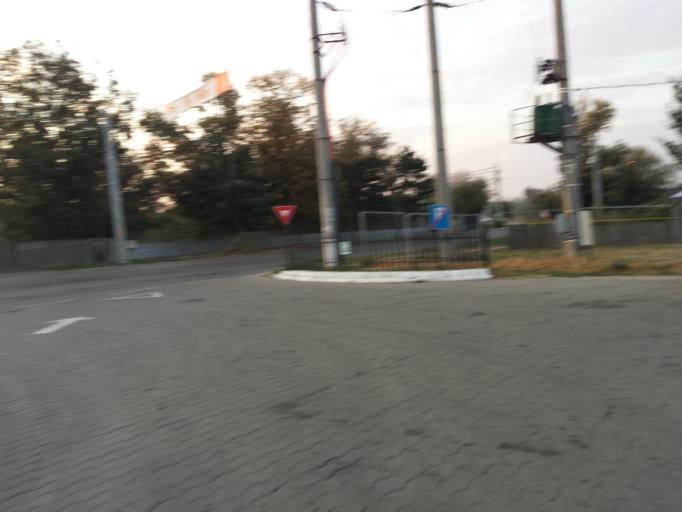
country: RO
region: Calarasi
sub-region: Municipiul Oltenita
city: Oltenita
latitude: 44.1078
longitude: 26.6387
